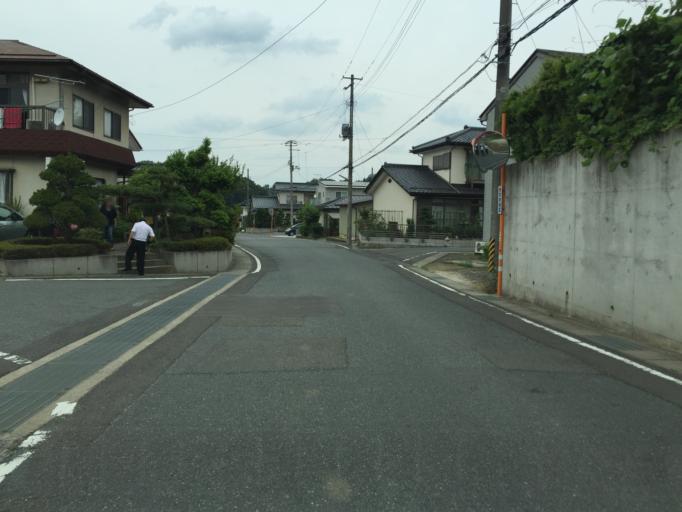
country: JP
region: Fukushima
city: Nihommatsu
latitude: 37.6576
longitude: 140.4782
